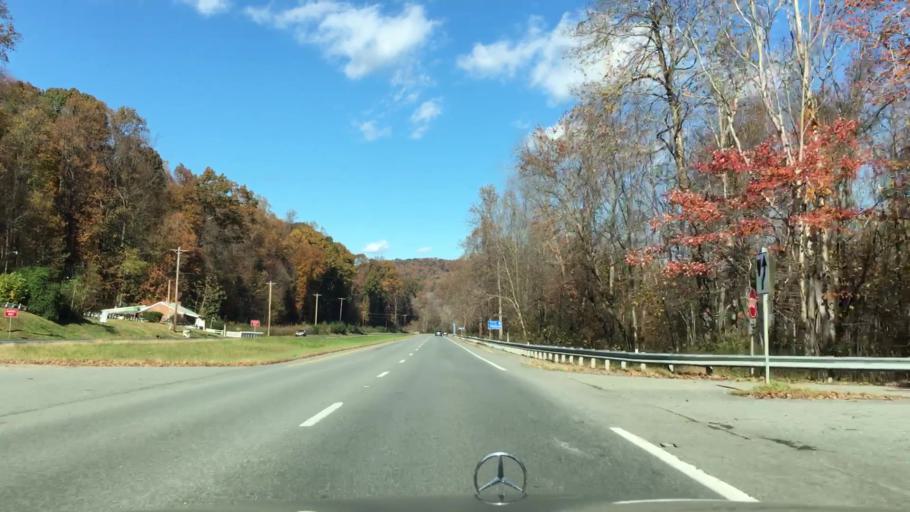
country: US
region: Virginia
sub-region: Albemarle County
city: Crozet
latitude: 37.9495
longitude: -78.6628
